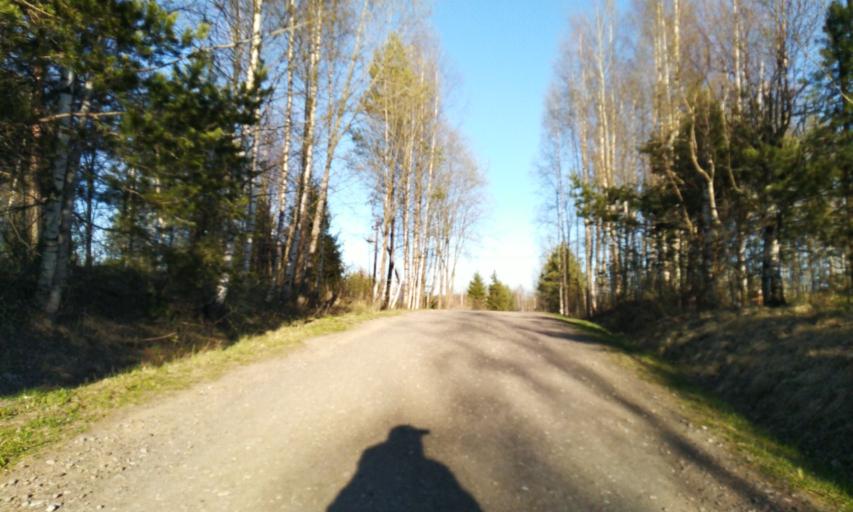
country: RU
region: Leningrad
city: Toksovo
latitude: 60.1522
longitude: 30.5794
